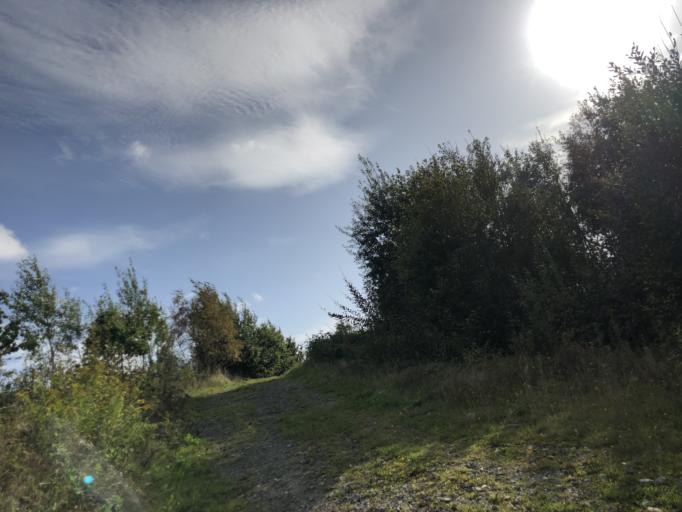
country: SE
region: Vaestra Goetaland
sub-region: Goteborg
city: Majorna
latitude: 57.7615
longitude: 11.8686
